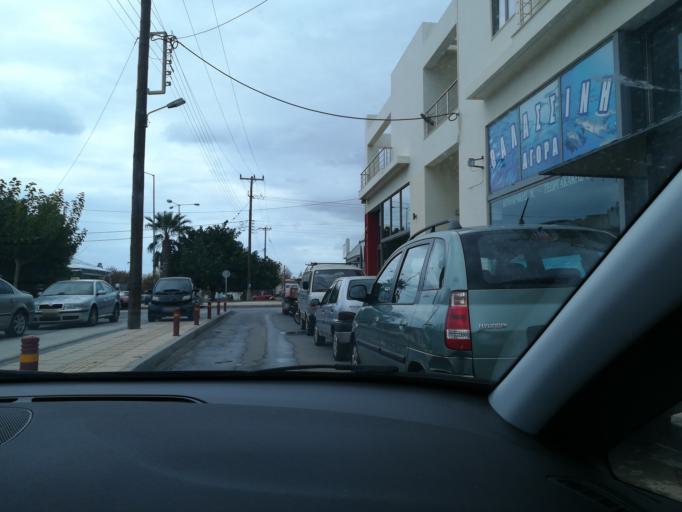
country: GR
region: Crete
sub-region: Nomos Lasithiou
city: Siteia
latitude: 35.2051
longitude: 26.1043
